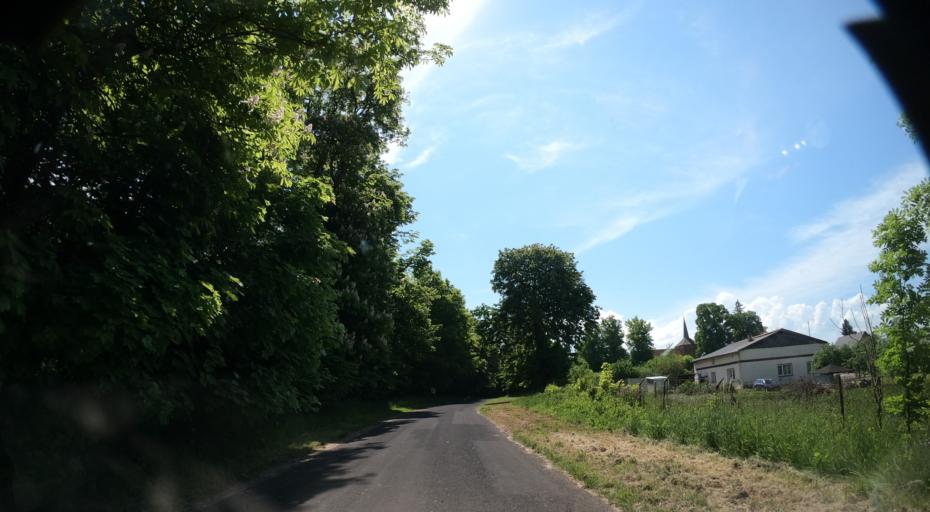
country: PL
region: West Pomeranian Voivodeship
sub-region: Powiat kolobrzeski
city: Ustronie Morskie
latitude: 54.1637
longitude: 15.8090
